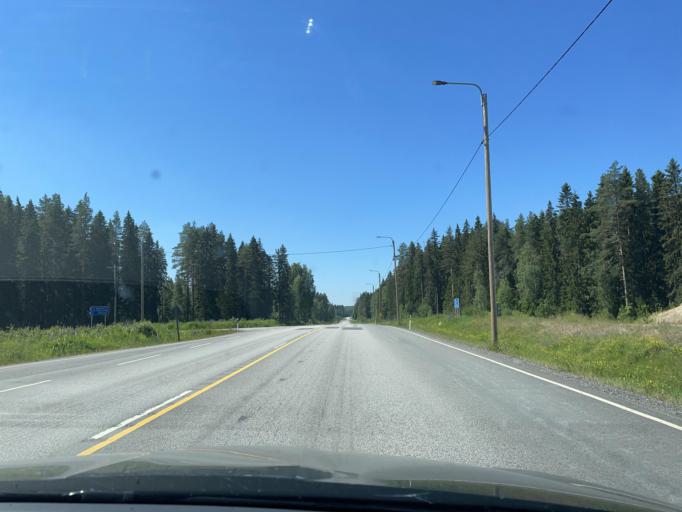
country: FI
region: Central Finland
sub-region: Saarijaervi-Viitasaari
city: Viitasaari
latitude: 63.1732
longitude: 26.0143
